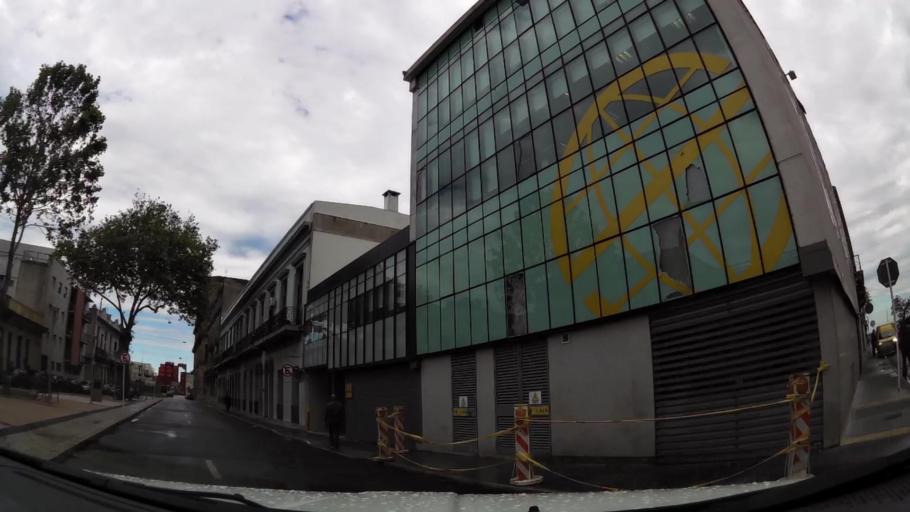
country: UY
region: Montevideo
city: Montevideo
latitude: -34.9074
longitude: -56.2131
